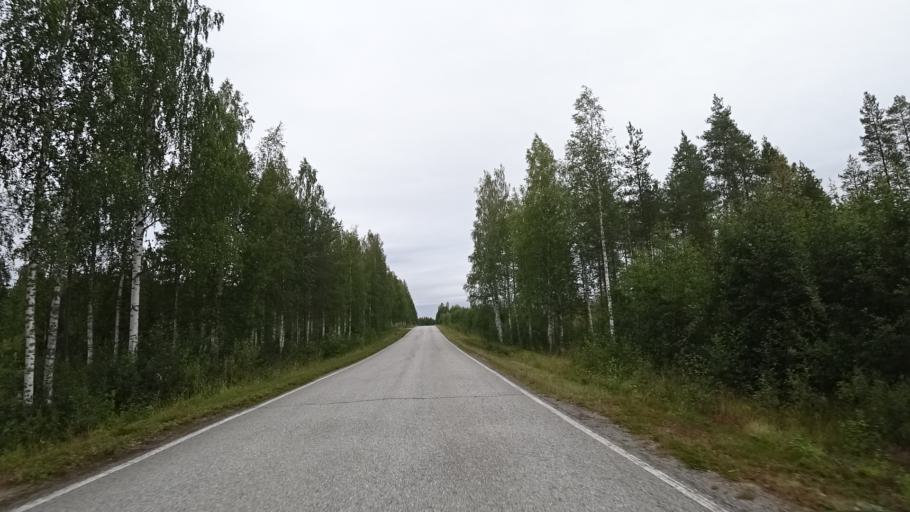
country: FI
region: North Karelia
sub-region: Pielisen Karjala
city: Lieksa
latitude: 63.3523
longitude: 30.2648
